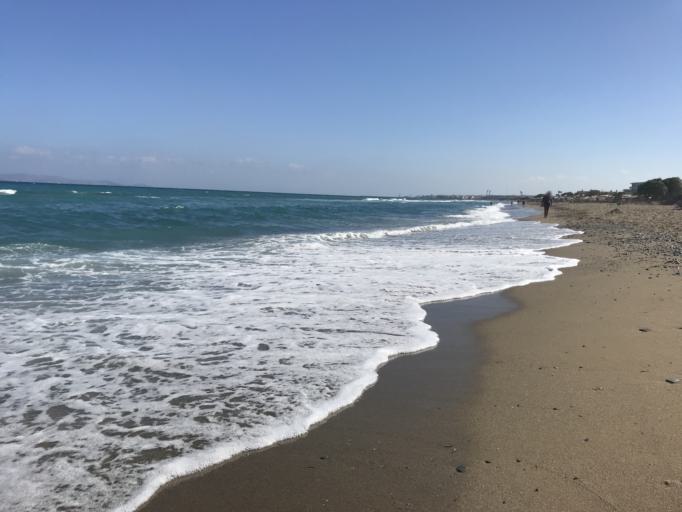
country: GR
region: Crete
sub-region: Nomos Irakleiou
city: Gazi
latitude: 35.3385
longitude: 25.0700
